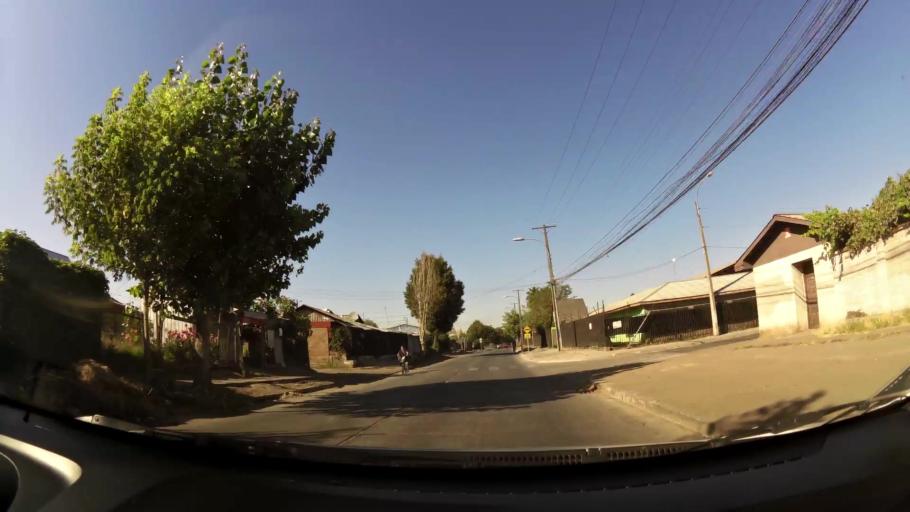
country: CL
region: Maule
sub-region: Provincia de Curico
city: Curico
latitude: -34.9912
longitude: -71.2539
